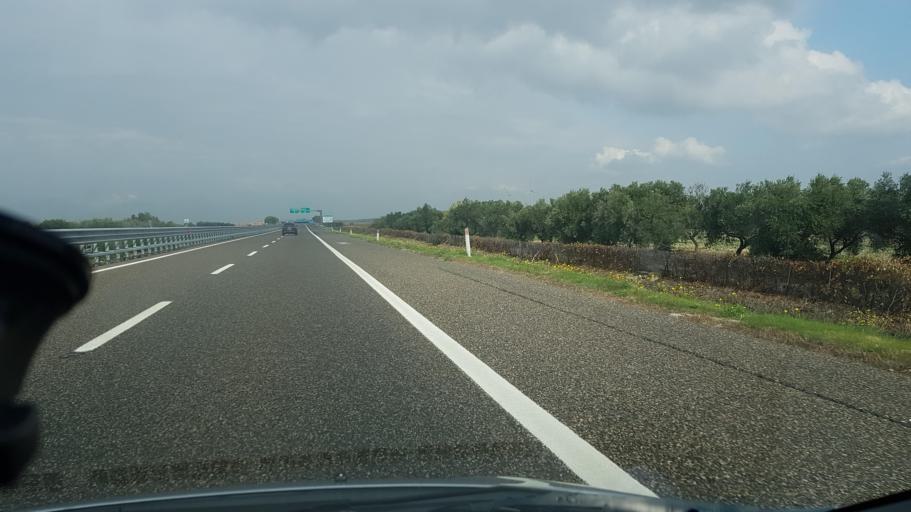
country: IT
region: Apulia
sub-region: Provincia di Foggia
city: Carapelle
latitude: 41.4174
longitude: 15.6649
